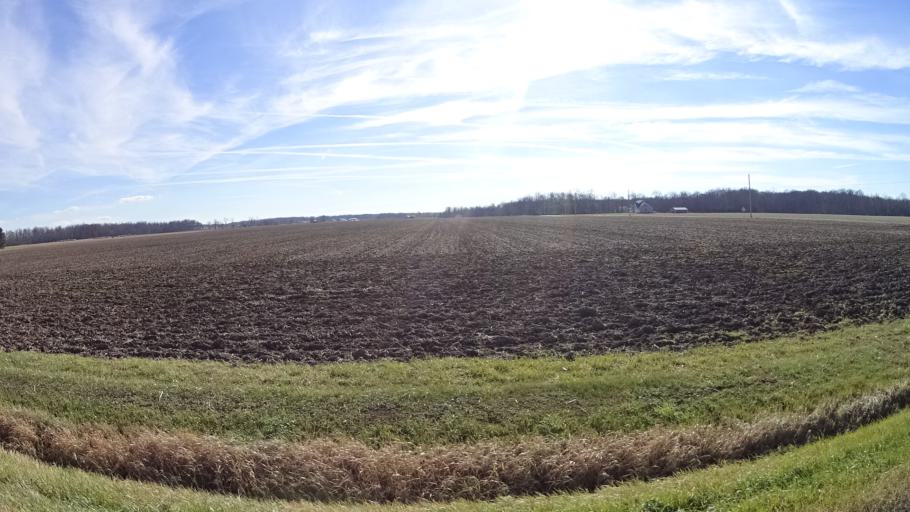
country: US
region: Ohio
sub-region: Lorain County
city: Wellington
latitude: 41.1012
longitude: -82.2387
